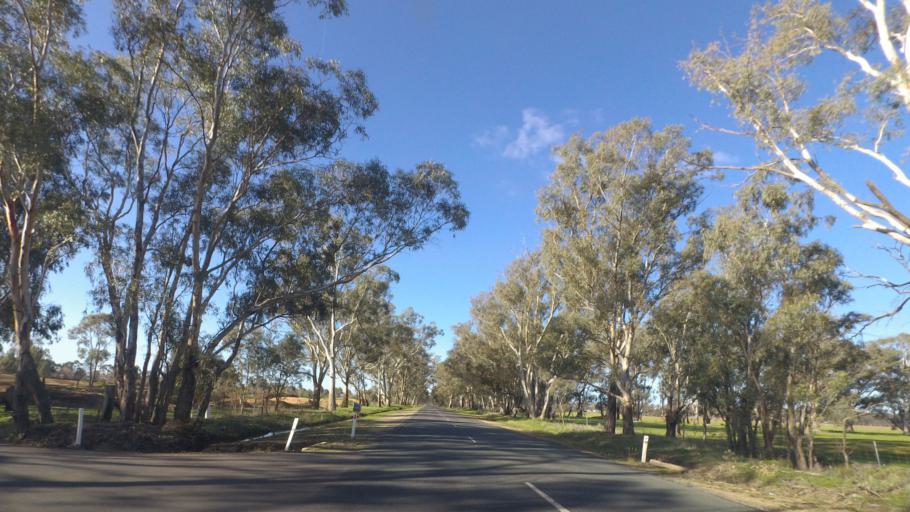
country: AU
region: Victoria
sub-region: Greater Bendigo
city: Epsom
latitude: -36.6611
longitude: 144.4605
